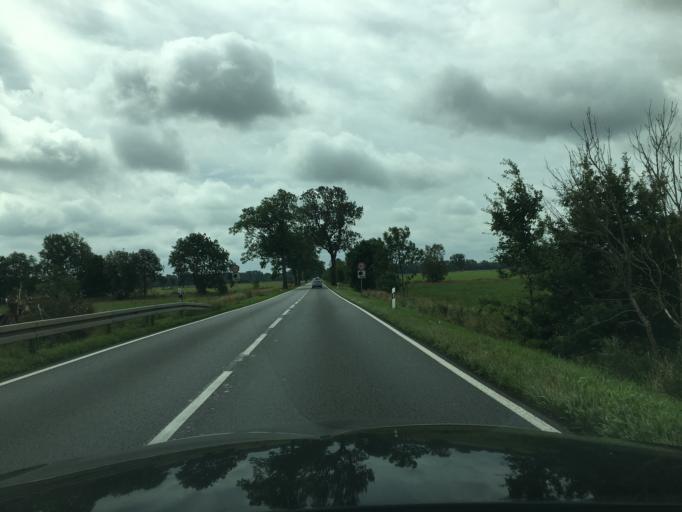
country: DE
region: Brandenburg
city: Oranienburg
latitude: 52.8425
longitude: 13.1958
